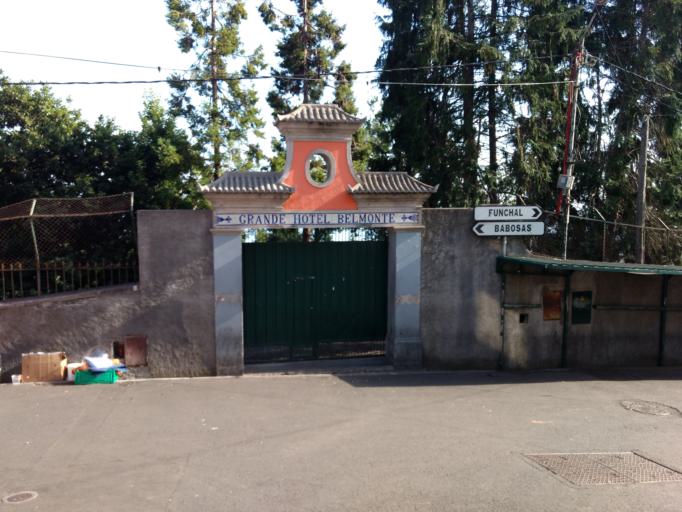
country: PT
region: Madeira
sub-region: Funchal
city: Nossa Senhora do Monte
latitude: 32.6754
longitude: -16.9026
